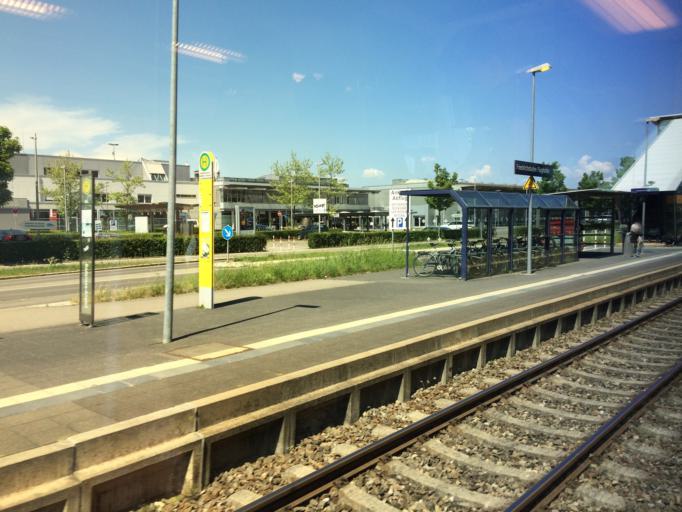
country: DE
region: Baden-Wuerttemberg
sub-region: Tuebingen Region
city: Friedrichshafen
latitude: 47.6720
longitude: 9.5232
